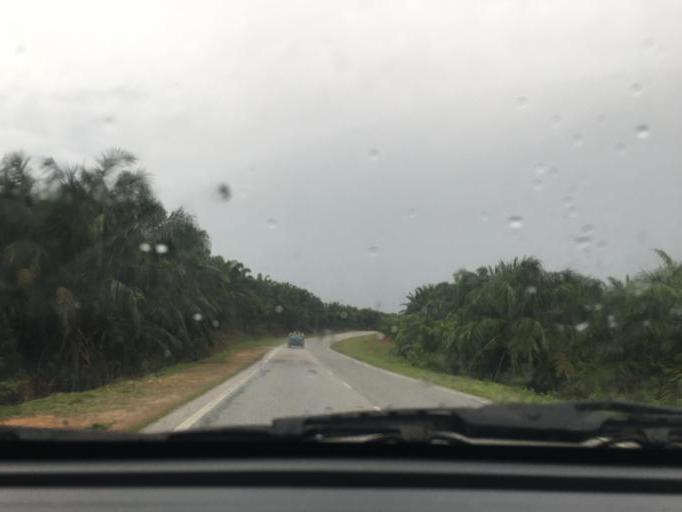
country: MY
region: Kedah
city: Sungai Petani
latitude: 5.6234
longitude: 100.6371
